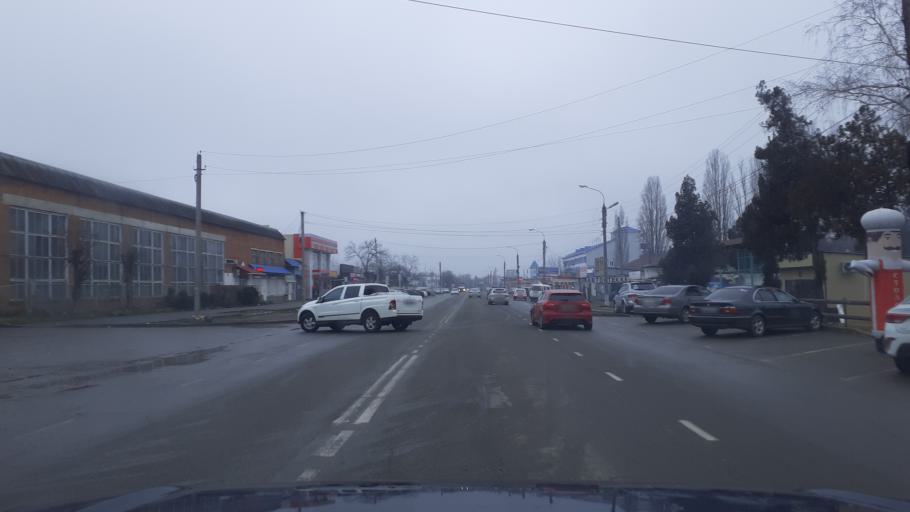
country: RU
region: Adygeya
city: Maykop
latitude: 44.6221
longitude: 40.0651
